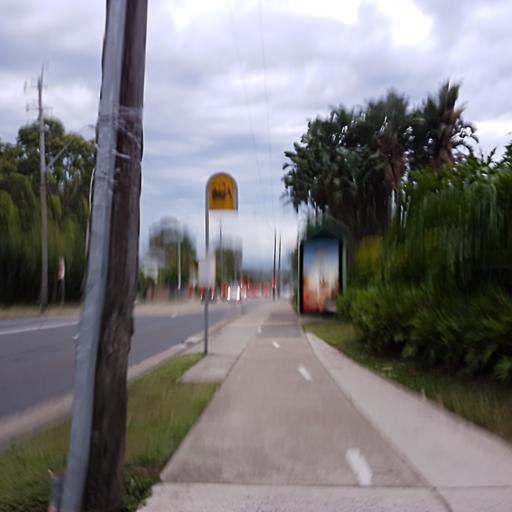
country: AU
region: New South Wales
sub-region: Warringah
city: Freshwater
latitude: -33.7828
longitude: 151.2802
